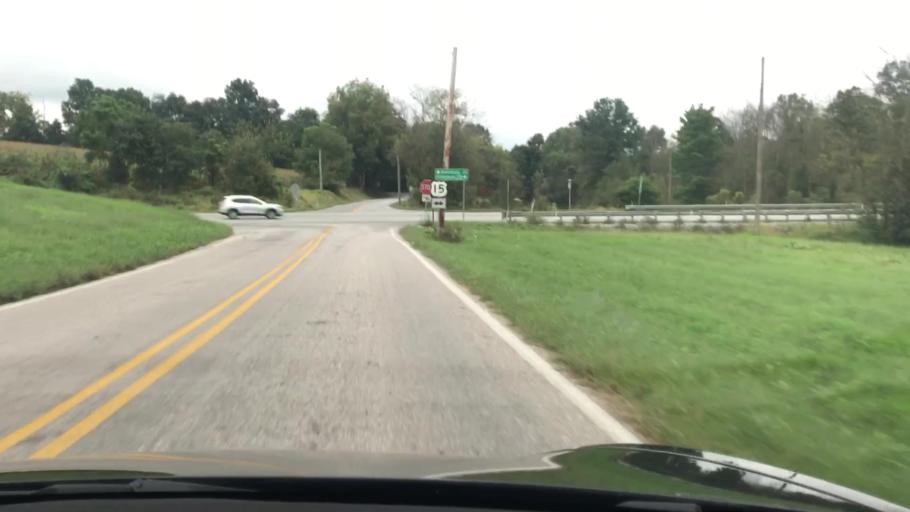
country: US
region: Pennsylvania
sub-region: York County
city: Dillsburg
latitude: 40.0584
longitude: -77.0677
